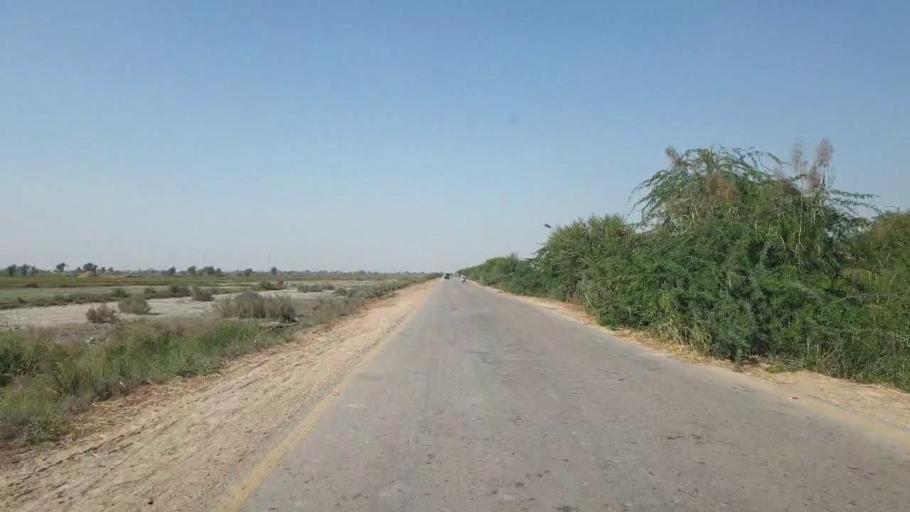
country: PK
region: Sindh
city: Rajo Khanani
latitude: 25.0492
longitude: 68.8090
